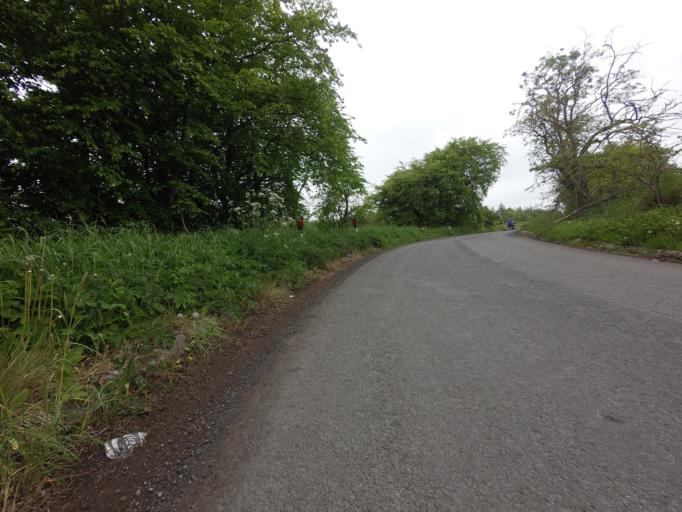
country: GB
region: Scotland
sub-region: Fife
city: Townhill
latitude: 56.1256
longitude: -3.4382
